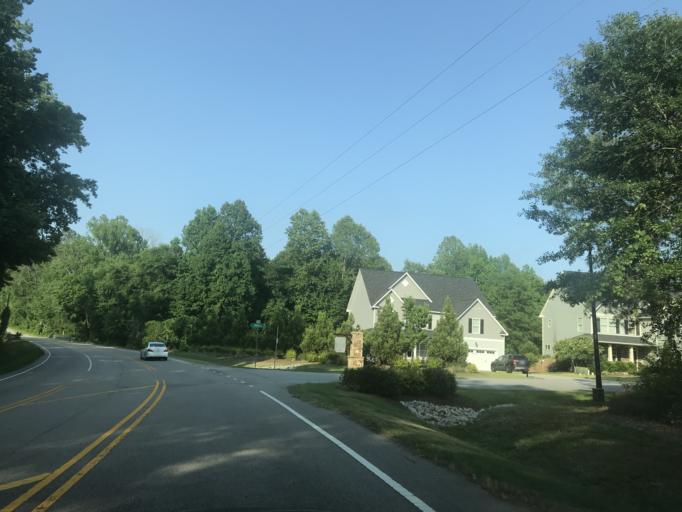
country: US
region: North Carolina
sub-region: Wake County
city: Knightdale
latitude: 35.8537
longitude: -78.4990
